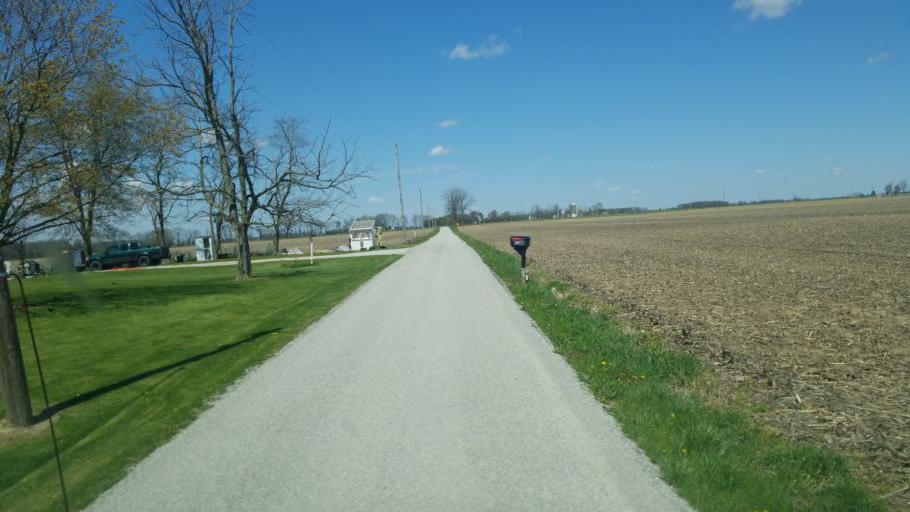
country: US
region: Ohio
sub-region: Marion County
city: Prospect
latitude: 40.3900
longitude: -83.1304
